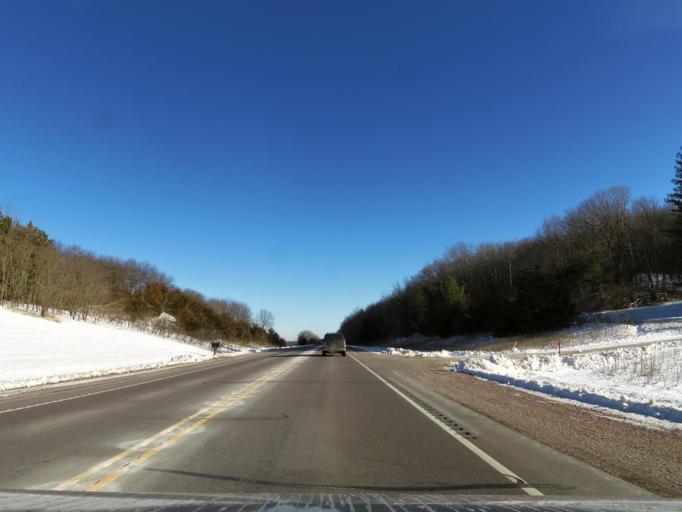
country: US
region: Wisconsin
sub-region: Columbia County
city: Portage
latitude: 43.5092
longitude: -89.5685
